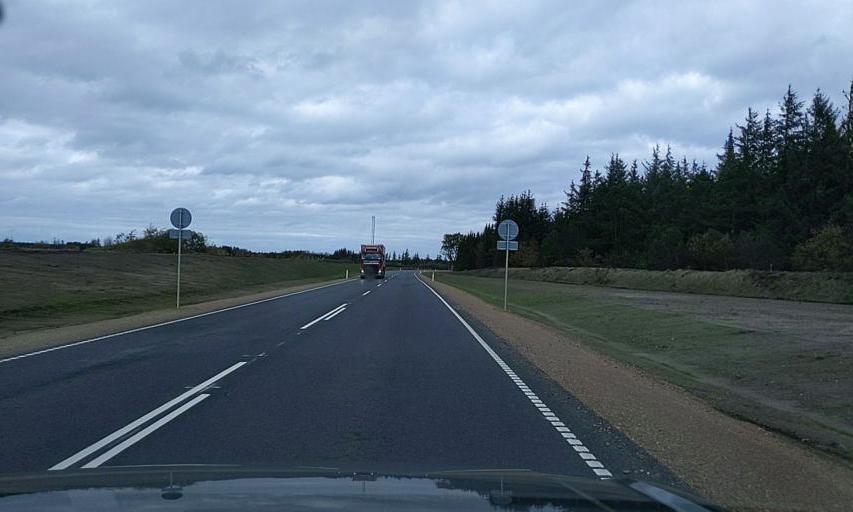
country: DK
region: Central Jutland
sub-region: Skive Kommune
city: Skive
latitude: 56.4227
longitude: 8.9691
